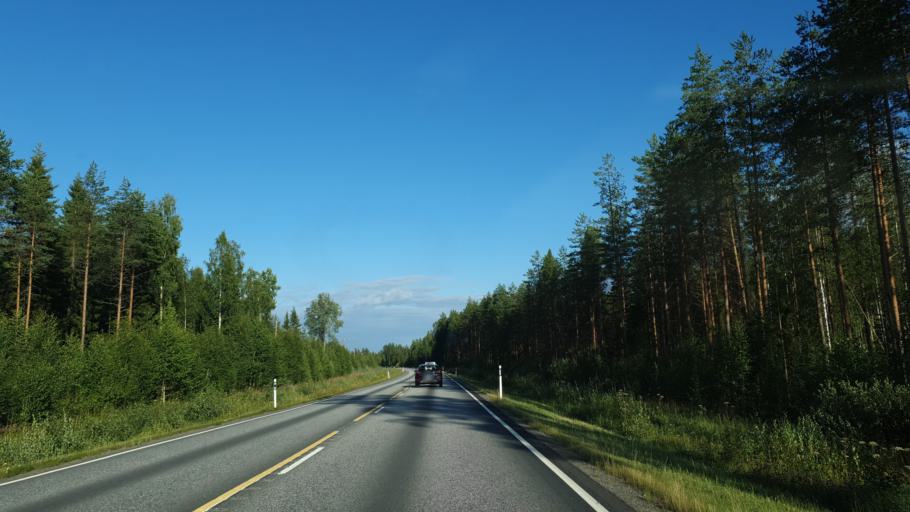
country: FI
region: North Karelia
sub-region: Joensuu
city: Outokumpu
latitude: 62.5341
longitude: 28.9532
